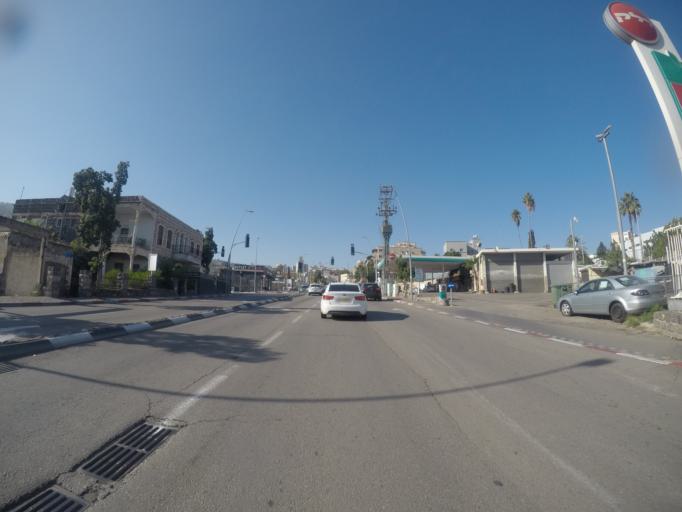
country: IL
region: Northern District
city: Tiberias
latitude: 32.7917
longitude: 35.5367
